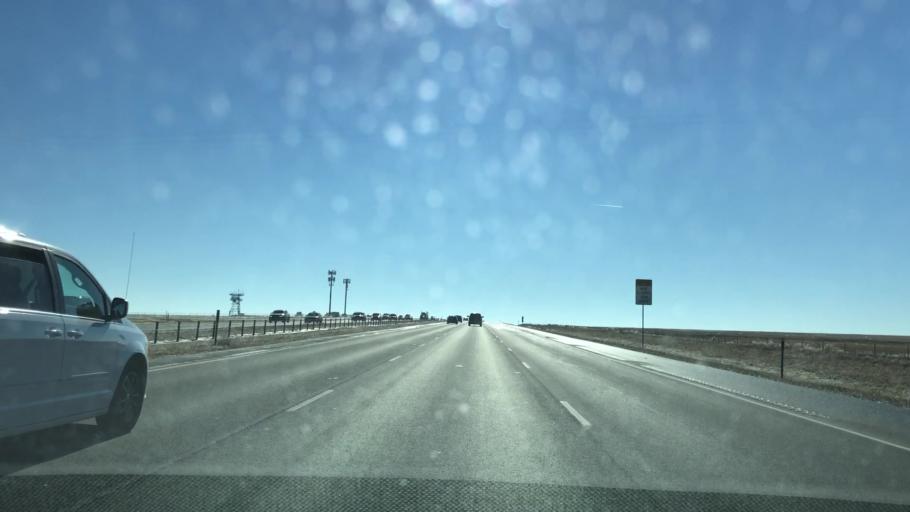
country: US
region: Colorado
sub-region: Weld County
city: Mead
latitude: 40.2750
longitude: -104.9803
